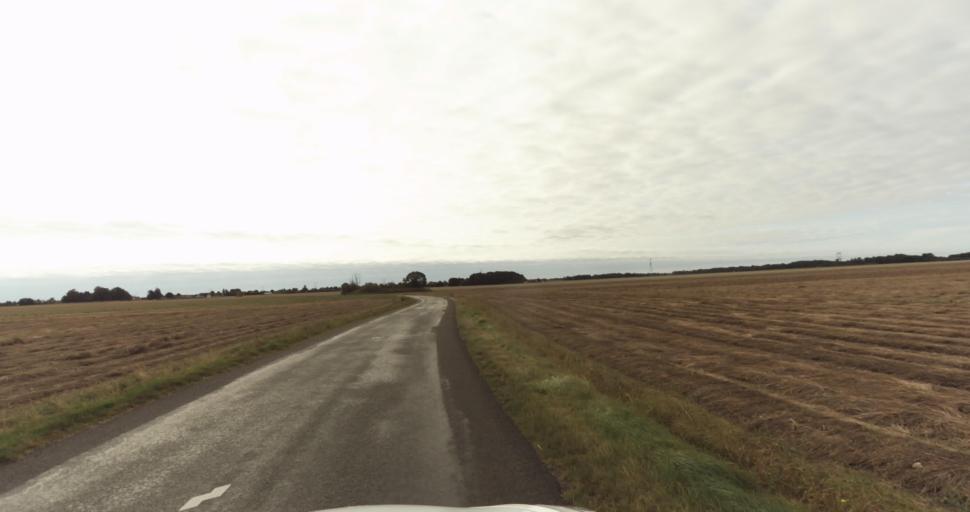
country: FR
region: Haute-Normandie
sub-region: Departement de l'Eure
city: La Madeleine-de-Nonancourt
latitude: 48.8673
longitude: 1.2314
